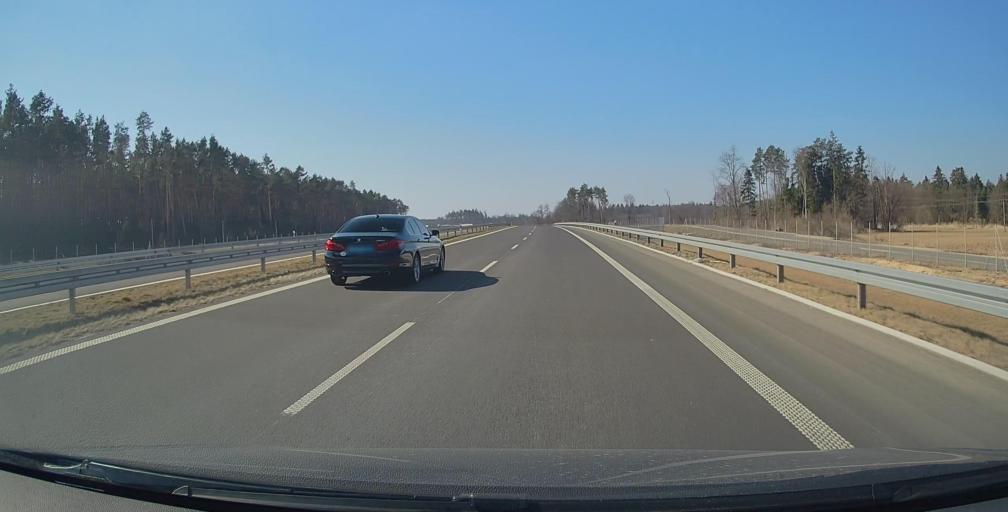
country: PL
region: Lublin Voivodeship
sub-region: Powiat janowski
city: Janow Lubelski
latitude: 50.6864
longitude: 22.3523
